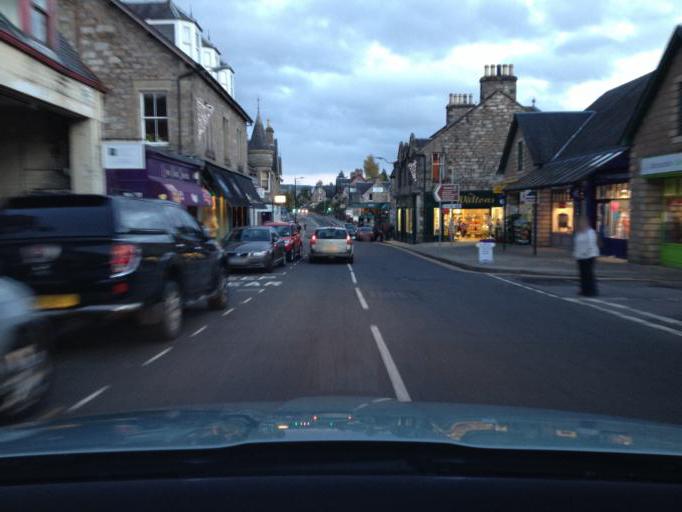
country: GB
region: Scotland
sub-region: Perth and Kinross
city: Pitlochry
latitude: 56.7029
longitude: -3.7336
